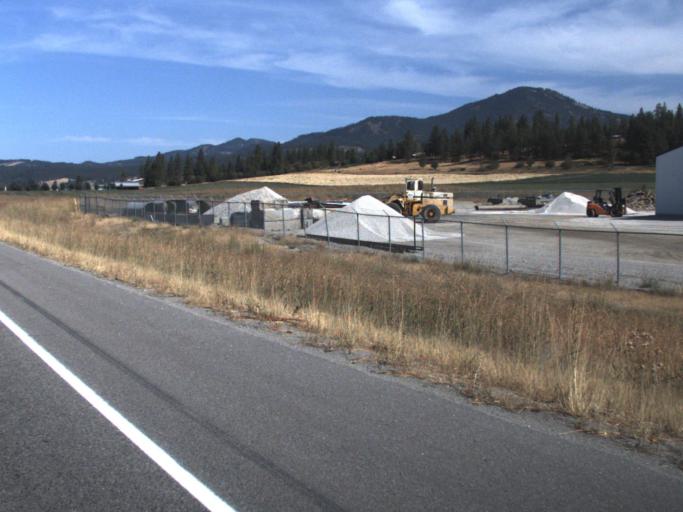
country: US
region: Washington
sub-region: Stevens County
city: Chewelah
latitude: 48.2526
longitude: -117.7153
